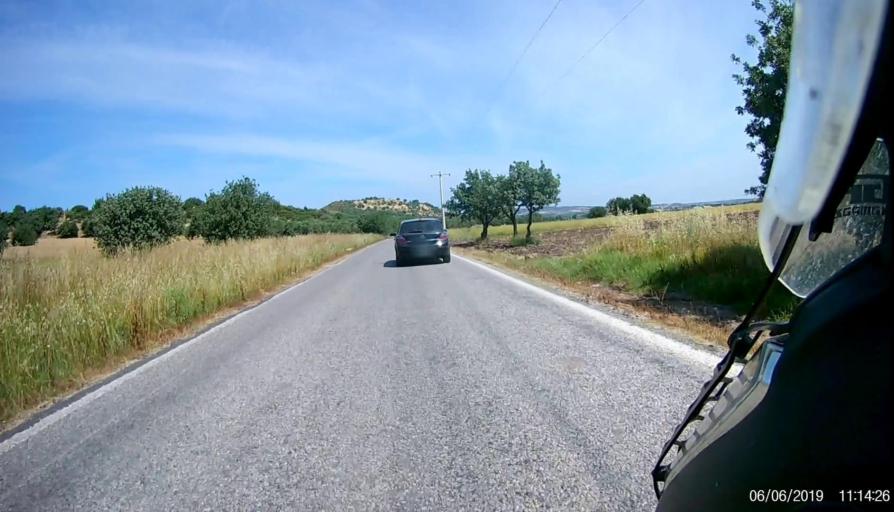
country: TR
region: Canakkale
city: Gulpinar
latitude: 39.6234
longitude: 26.1763
